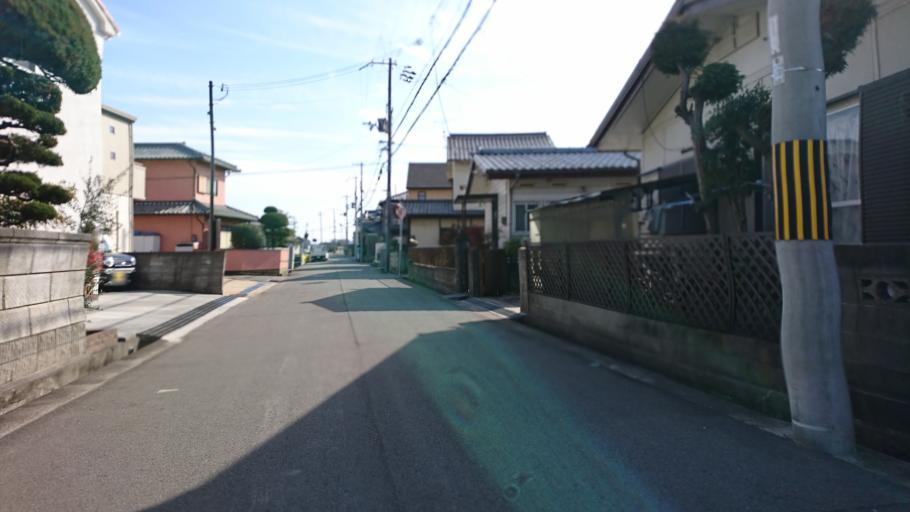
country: JP
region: Hyogo
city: Kakogawacho-honmachi
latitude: 34.7857
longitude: 134.8342
